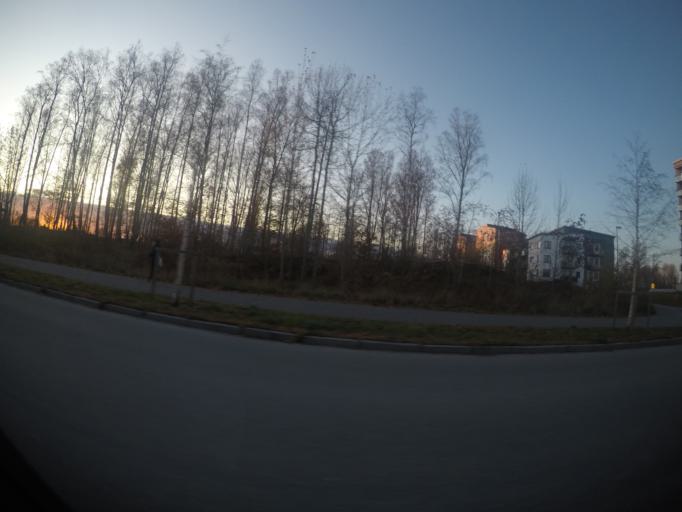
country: SE
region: OErebro
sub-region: Orebro Kommun
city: Orebro
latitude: 59.2843
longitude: 15.2378
